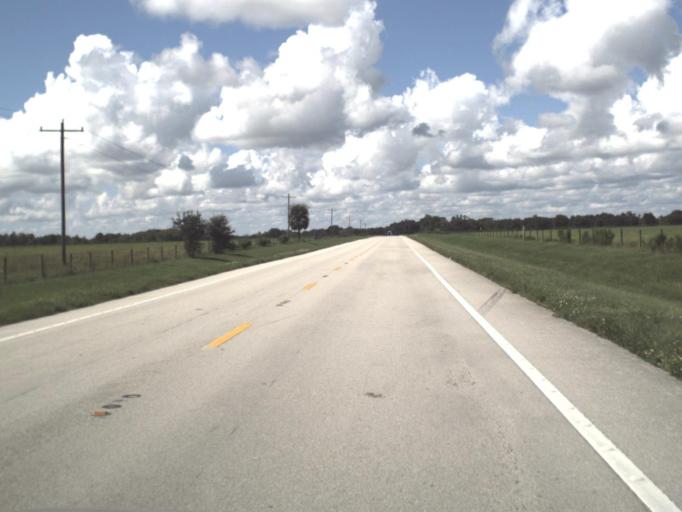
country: US
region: Florida
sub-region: DeSoto County
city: Arcadia
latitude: 27.2457
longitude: -81.9500
